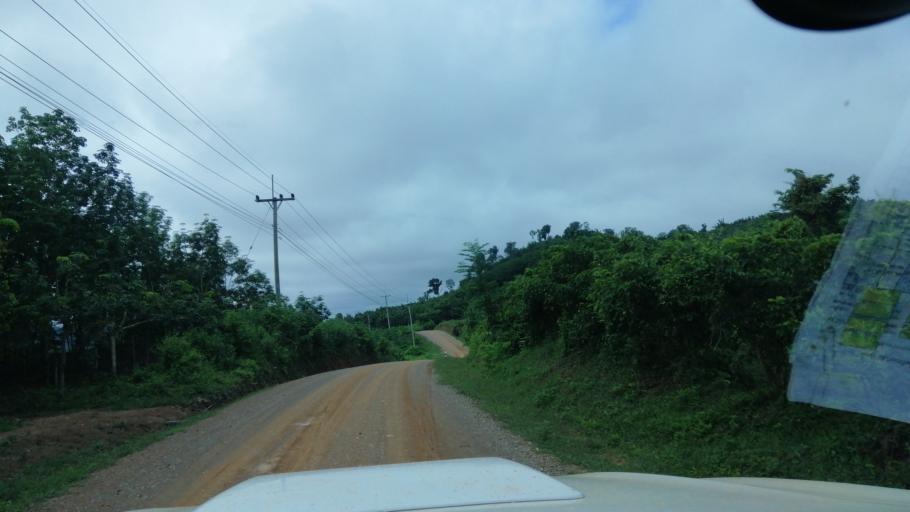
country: LA
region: Xiagnabouli
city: Muang Kenthao
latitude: 17.9836
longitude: 101.4164
